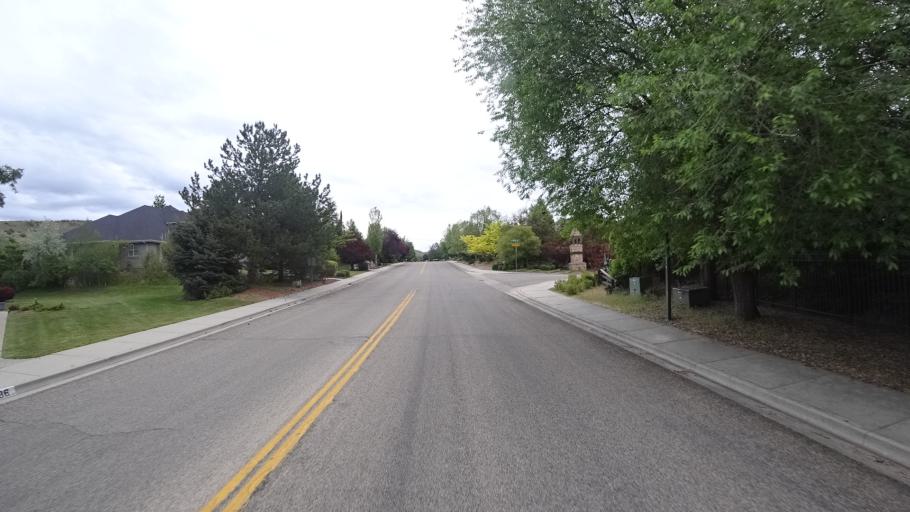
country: US
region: Idaho
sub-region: Ada County
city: Boise
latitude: 43.6119
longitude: -116.1561
